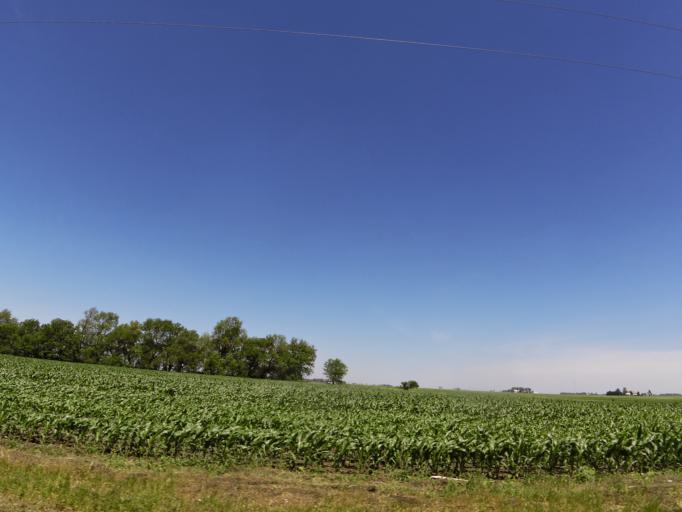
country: US
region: Illinois
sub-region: Iroquois County
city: Watseka
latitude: 40.6839
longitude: -87.8022
